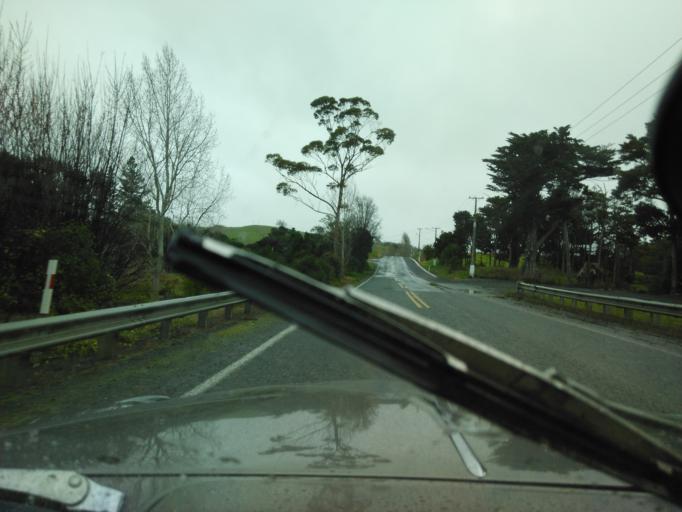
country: NZ
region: Auckland
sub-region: Auckland
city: Wellsford
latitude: -36.3761
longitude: 174.4533
